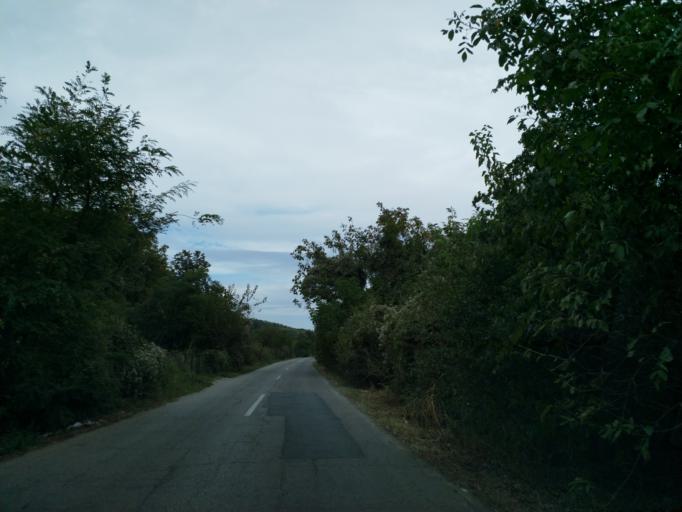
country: RS
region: Central Serbia
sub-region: Pomoravski Okrug
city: Paracin
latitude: 43.8451
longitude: 21.3223
